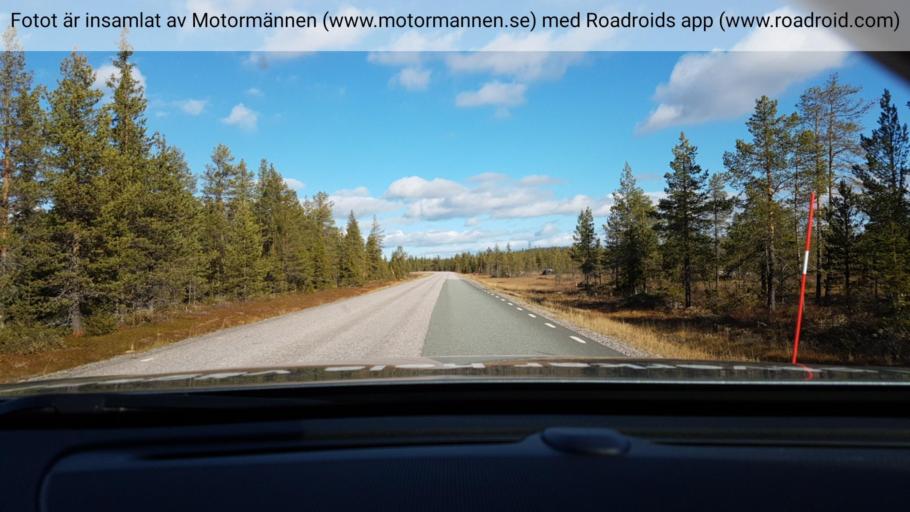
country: SE
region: Norrbotten
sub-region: Arjeplogs Kommun
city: Arjeplog
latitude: 65.8627
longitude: 18.4074
